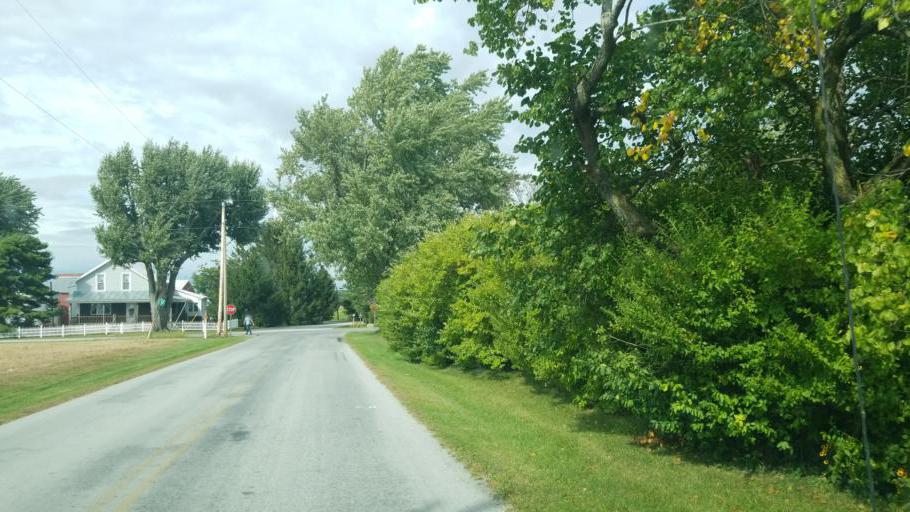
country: US
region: Ohio
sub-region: Hancock County
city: Arlington
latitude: 40.7898
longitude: -83.6518
